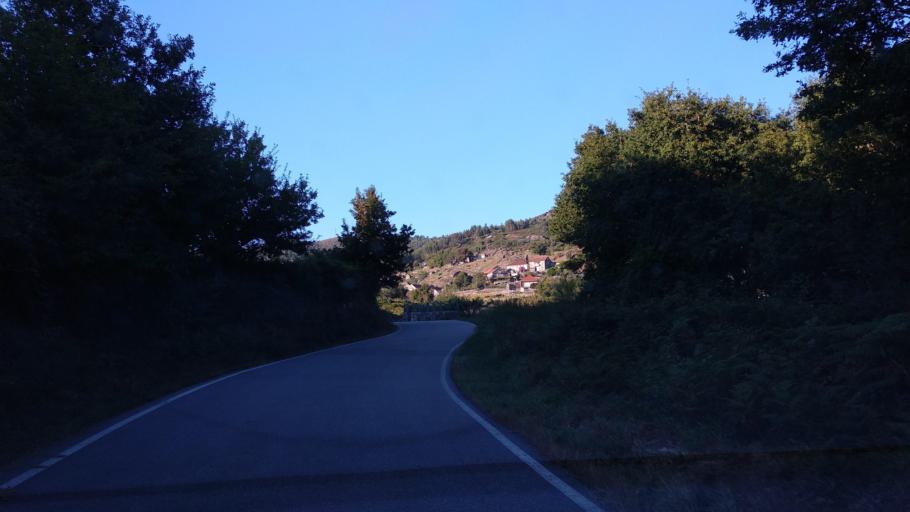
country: ES
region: Galicia
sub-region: Provincia de Pontevedra
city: Ponte Caldelas
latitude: 42.3553
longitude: -8.4914
